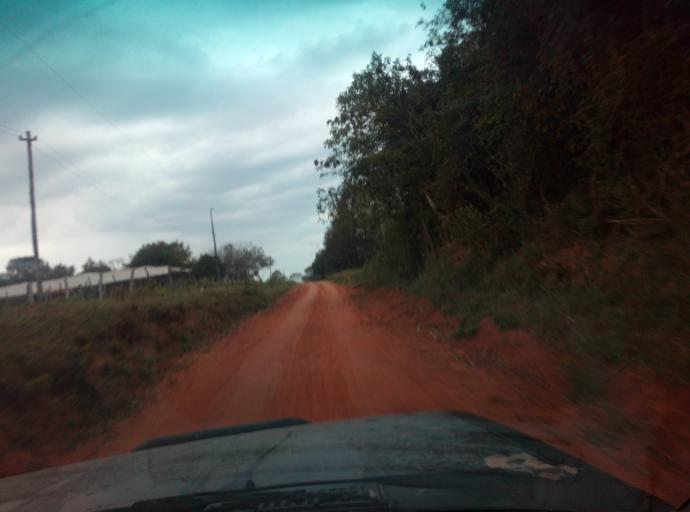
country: PY
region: Caaguazu
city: Doctor Cecilio Baez
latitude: -25.1396
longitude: -56.2237
